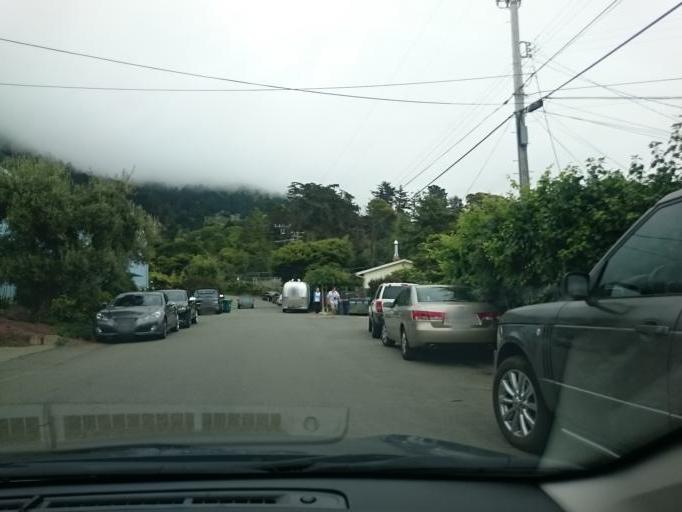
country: US
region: California
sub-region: Marin County
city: Bolinas
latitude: 37.8978
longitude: -122.6386
